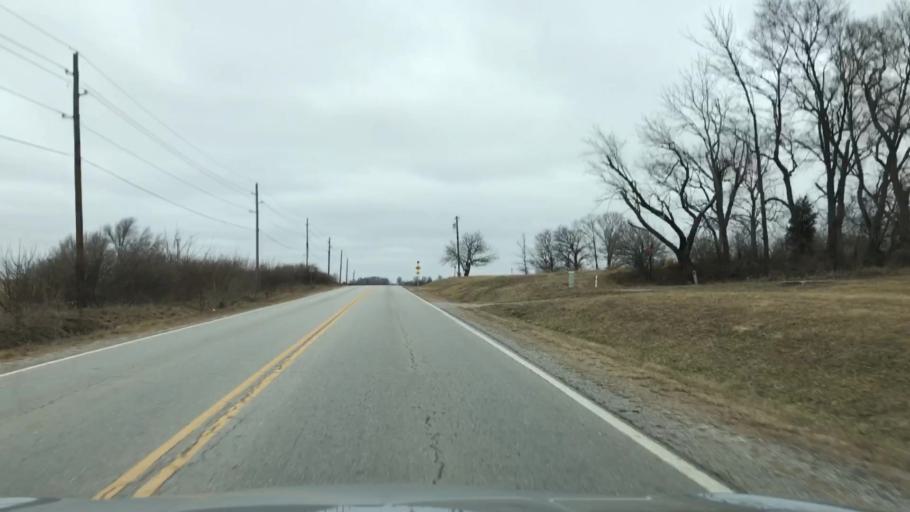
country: US
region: Missouri
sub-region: Clay County
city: Liberty
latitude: 39.2734
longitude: -94.4166
